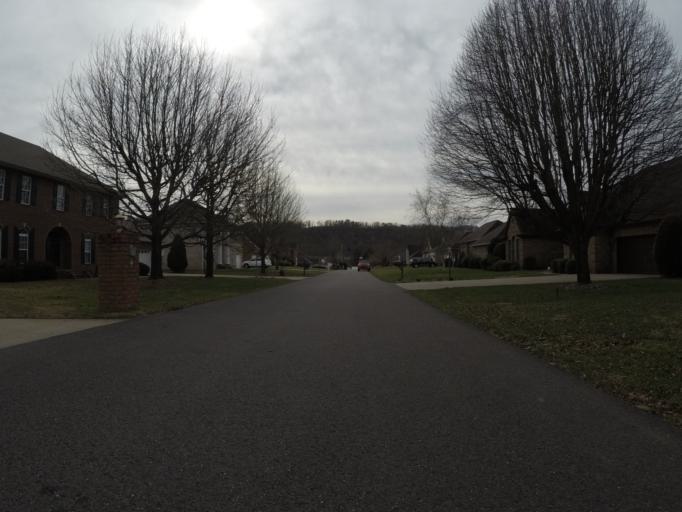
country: US
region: West Virginia
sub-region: Cabell County
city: Pea Ridge
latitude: 38.4435
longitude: -82.3499
